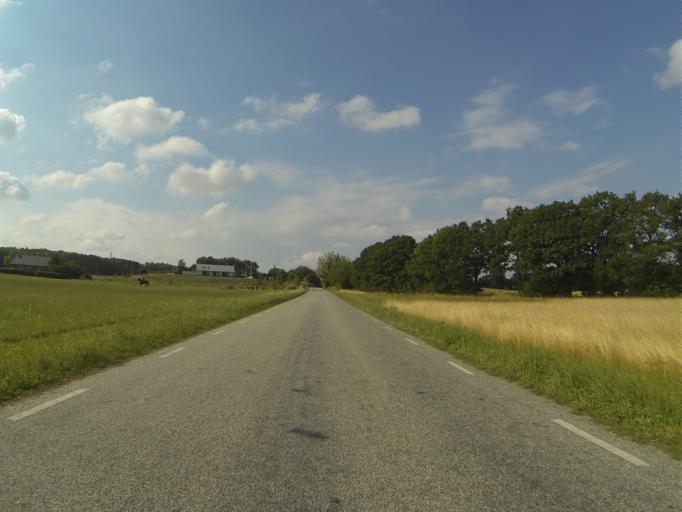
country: SE
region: Skane
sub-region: Lunds Kommun
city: Lund
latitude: 55.7299
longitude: 13.2994
